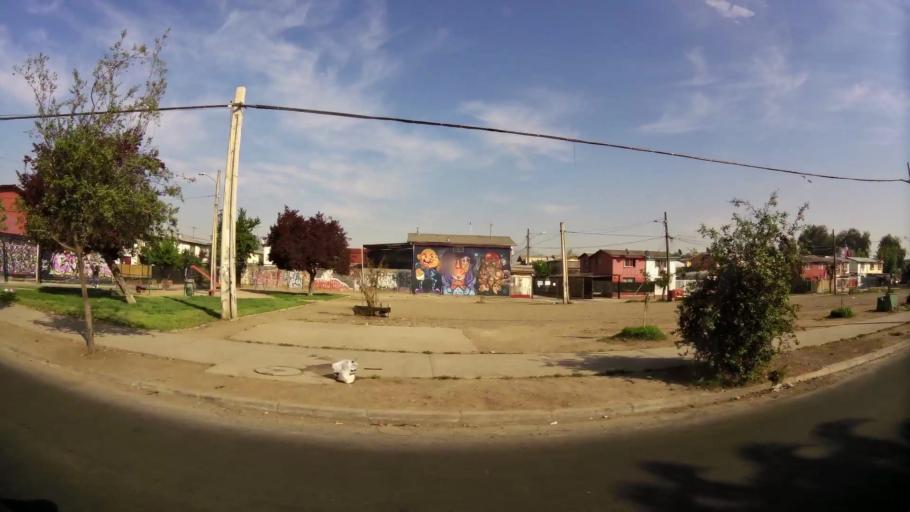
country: CL
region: Santiago Metropolitan
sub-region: Provincia de Santiago
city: Lo Prado
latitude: -33.4566
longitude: -70.7516
